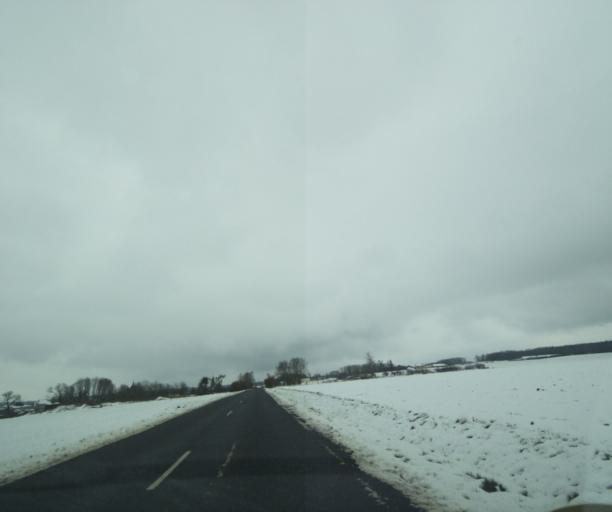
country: FR
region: Champagne-Ardenne
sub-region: Departement de la Haute-Marne
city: Laneuville-a-Remy
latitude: 48.4140
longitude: 4.8316
